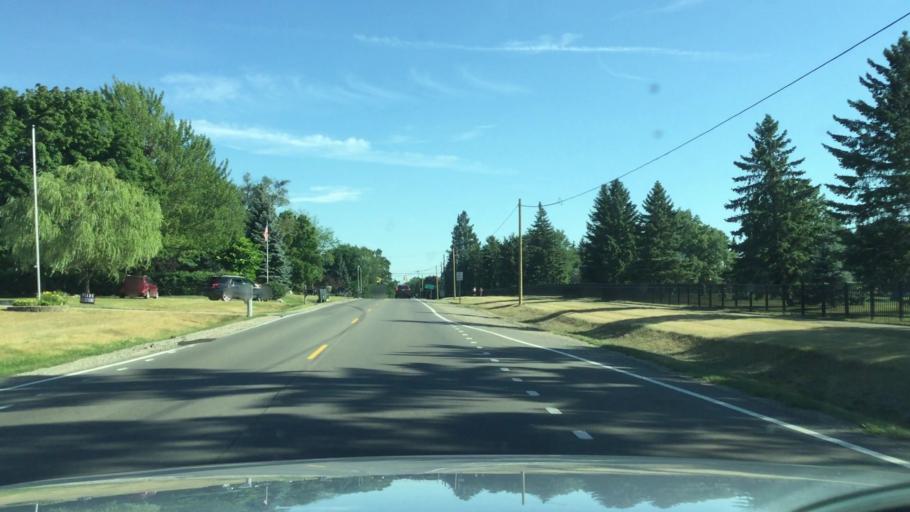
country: US
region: Michigan
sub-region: Oakland County
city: Waterford
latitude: 42.6699
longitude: -83.3867
